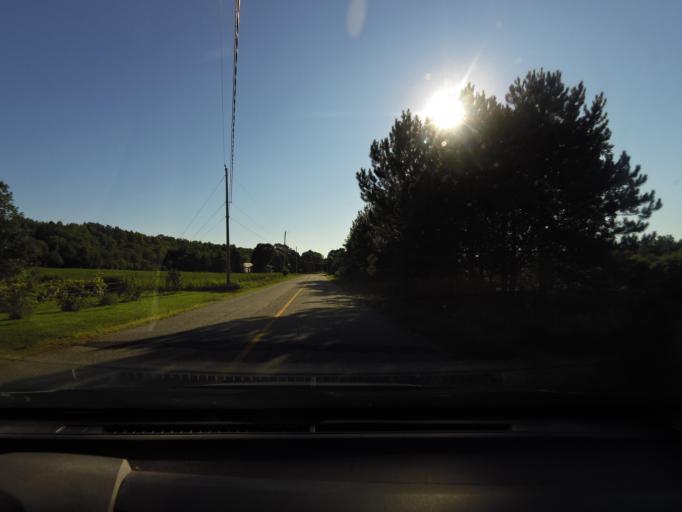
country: CA
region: Quebec
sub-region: Mauricie
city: Becancour
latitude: 46.5525
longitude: -72.3761
